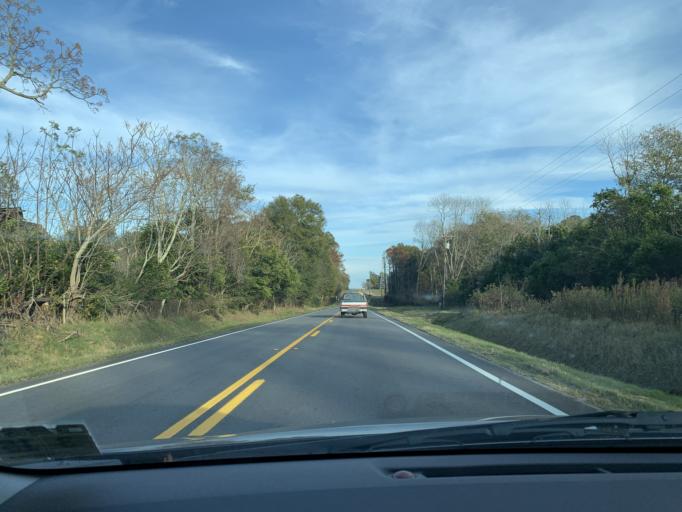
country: US
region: Georgia
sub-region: Irwin County
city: Ocilla
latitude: 31.5926
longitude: -83.1982
